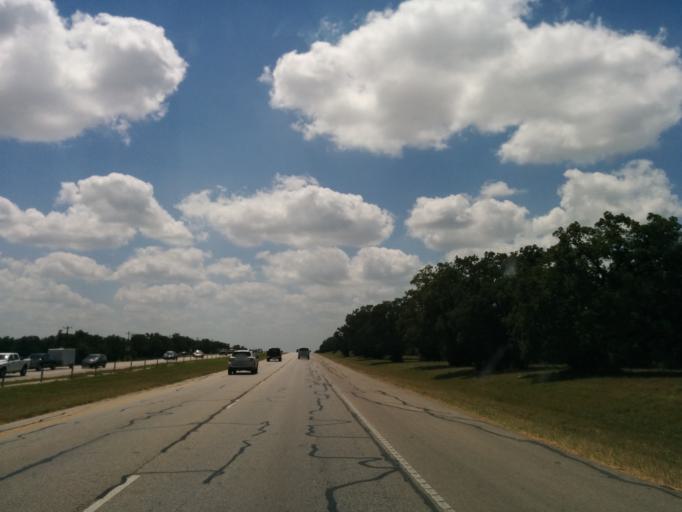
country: US
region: Texas
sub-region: Bastrop County
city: Bastrop
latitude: 30.1110
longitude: -97.3859
